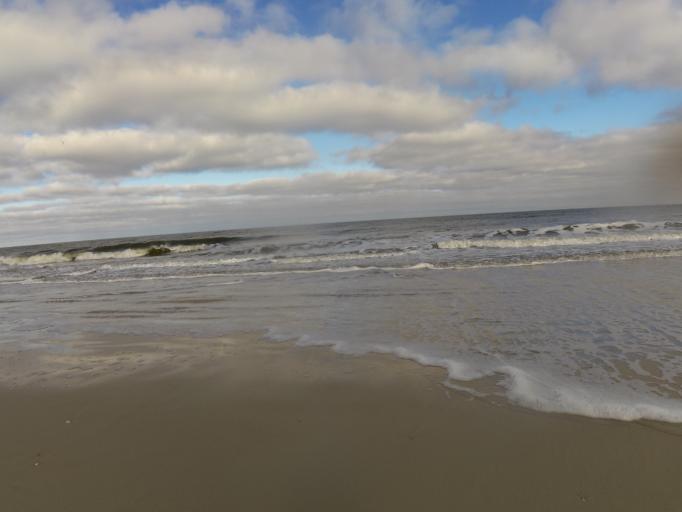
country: US
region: Florida
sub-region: Nassau County
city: Fernandina Beach
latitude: 30.5586
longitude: -81.4422
